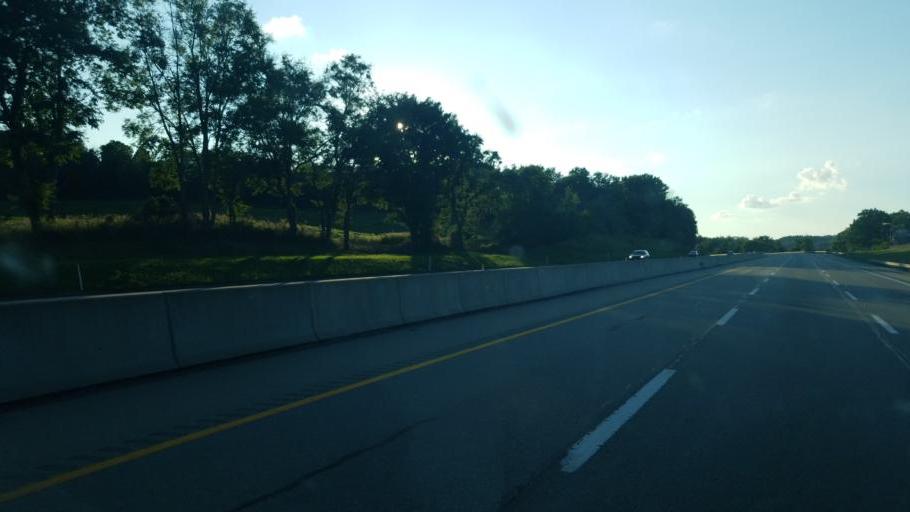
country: US
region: Pennsylvania
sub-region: Lawrence County
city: New Beaver
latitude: 40.8835
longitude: -80.4264
